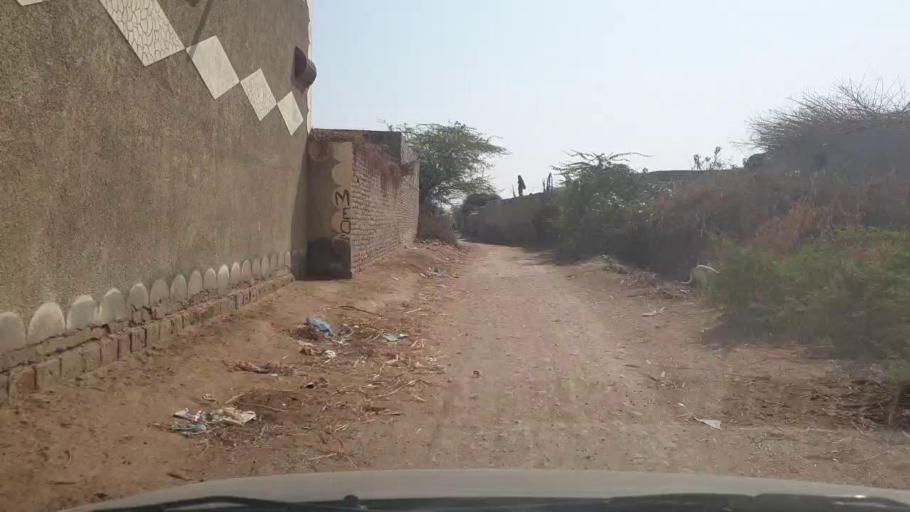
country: PK
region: Sindh
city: Mirwah Gorchani
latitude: 25.2523
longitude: 69.1200
